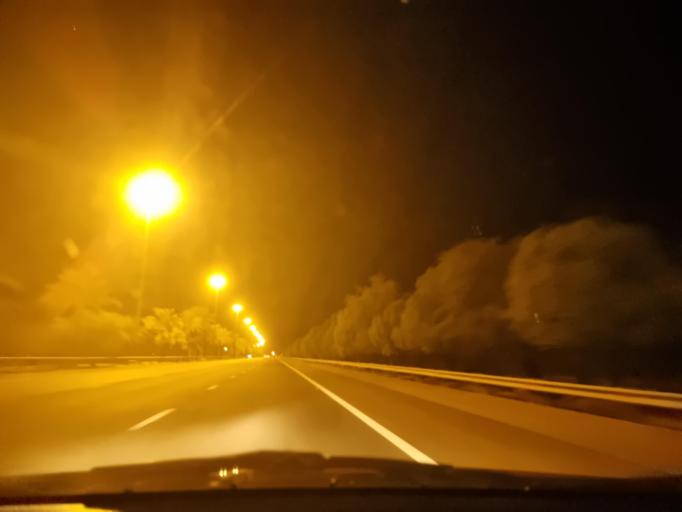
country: AE
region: Abu Dhabi
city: Al Ain
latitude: 24.2021
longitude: 55.3775
